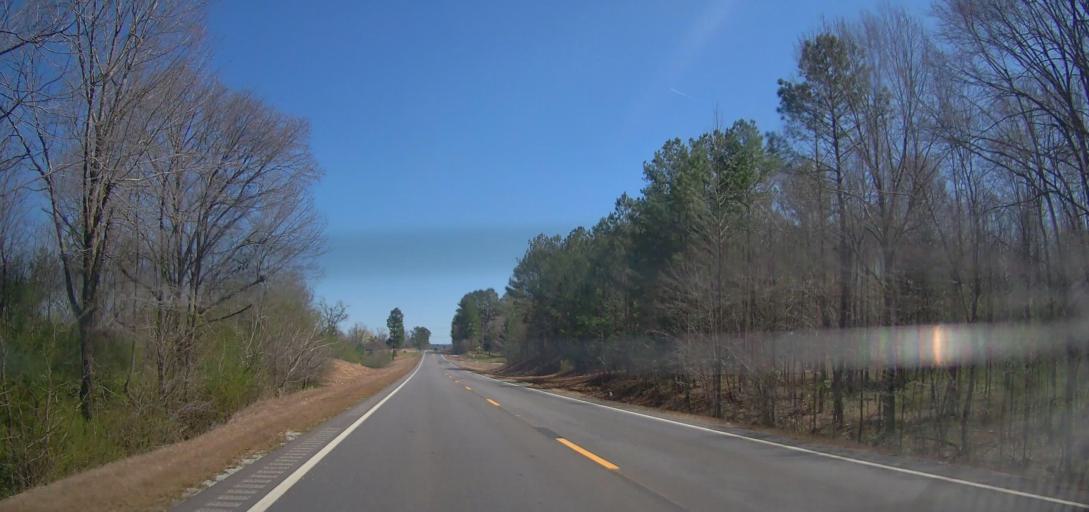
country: US
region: Alabama
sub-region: Calhoun County
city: Ohatchee
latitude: 33.7840
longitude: -85.9445
